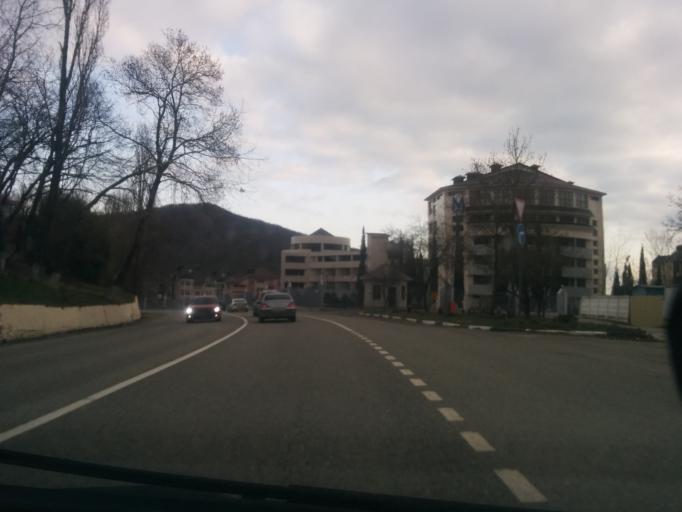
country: RU
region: Krasnodarskiy
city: Agoy
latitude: 44.1414
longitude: 39.0230
